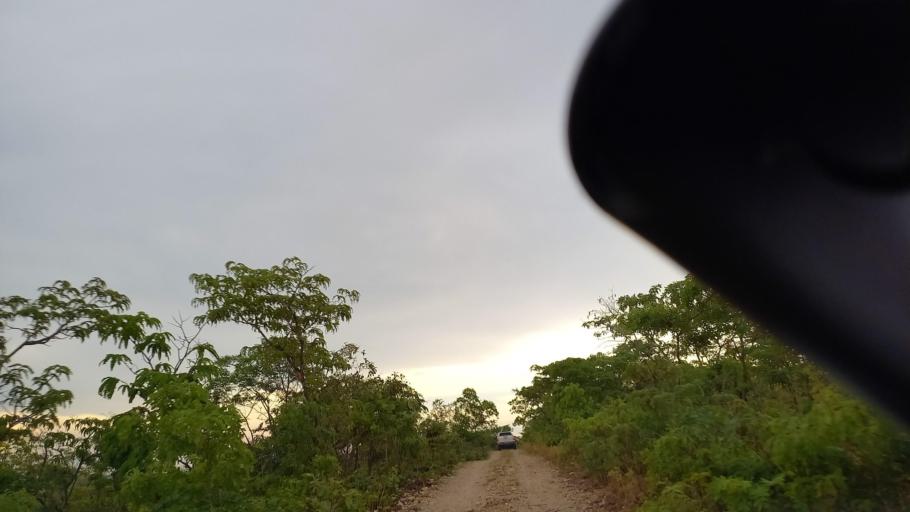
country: ZM
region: Lusaka
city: Kafue
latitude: -16.0466
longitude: 28.3191
